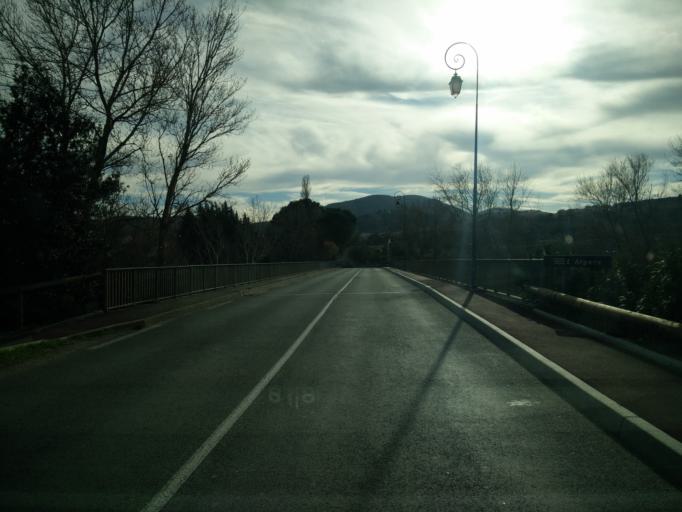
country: FR
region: Provence-Alpes-Cote d'Azur
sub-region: Departement du Var
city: Roquebrune-sur-Argens
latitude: 43.4504
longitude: 6.6330
